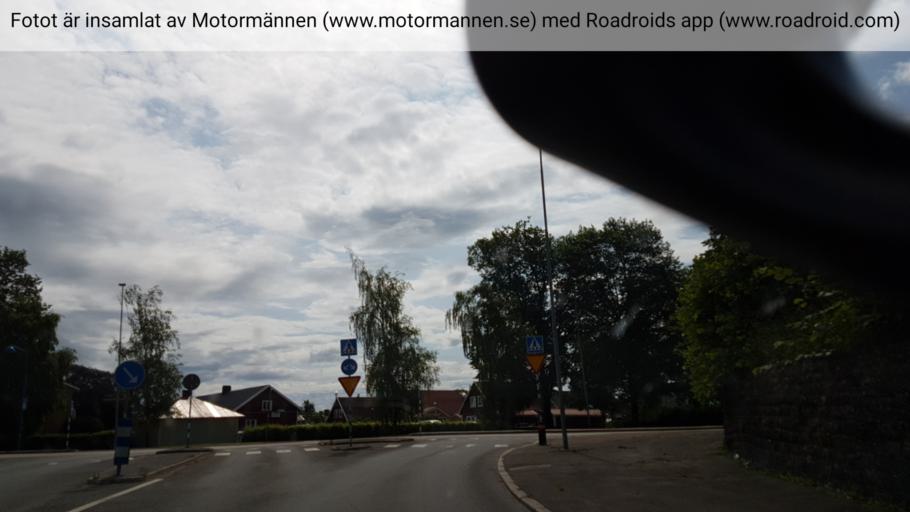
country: SE
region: Vaestra Goetaland
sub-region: Falkopings Kommun
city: Falkoeping
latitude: 58.1786
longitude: 13.5558
